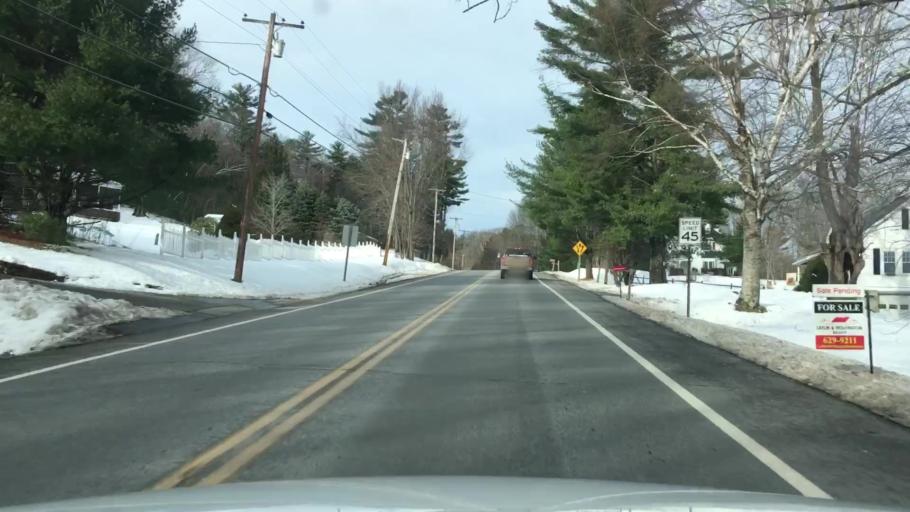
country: US
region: Maine
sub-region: Kennebec County
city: Winthrop
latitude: 44.3181
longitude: -69.9779
